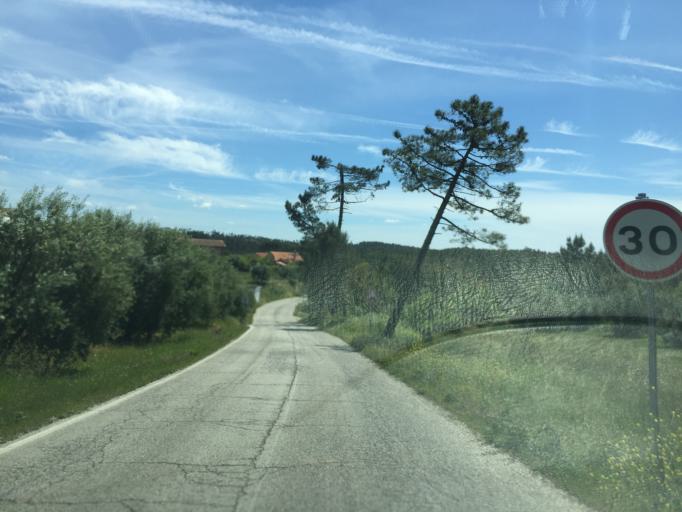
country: PT
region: Coimbra
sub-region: Soure
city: Soure
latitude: 40.0530
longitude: -8.6749
